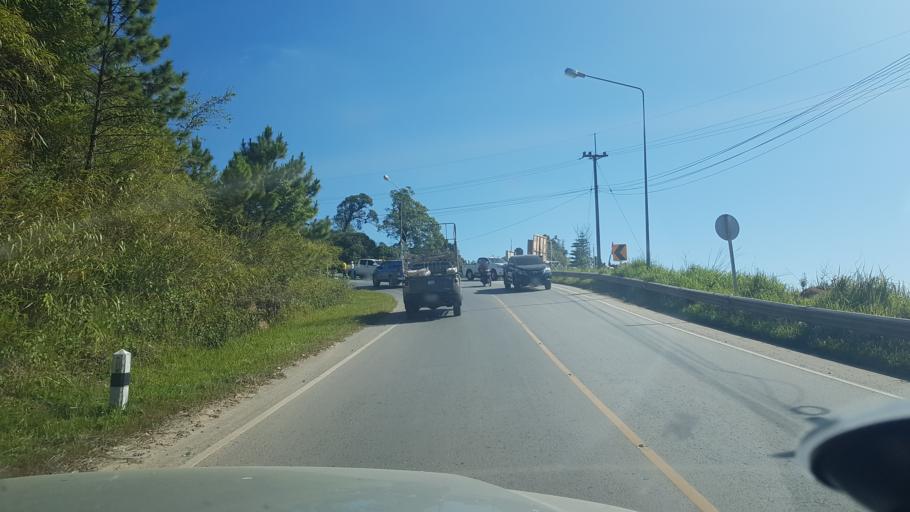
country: TH
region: Phetchabun
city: Lom Kao
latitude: 16.8924
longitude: 101.0983
